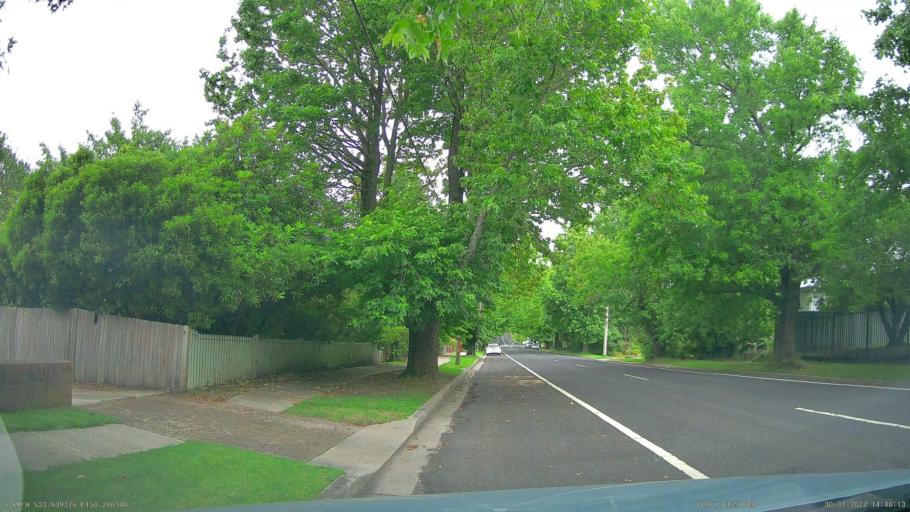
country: AU
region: New South Wales
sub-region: Blue Mountains Municipality
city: Blackheath
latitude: -33.6393
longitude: 150.2865
